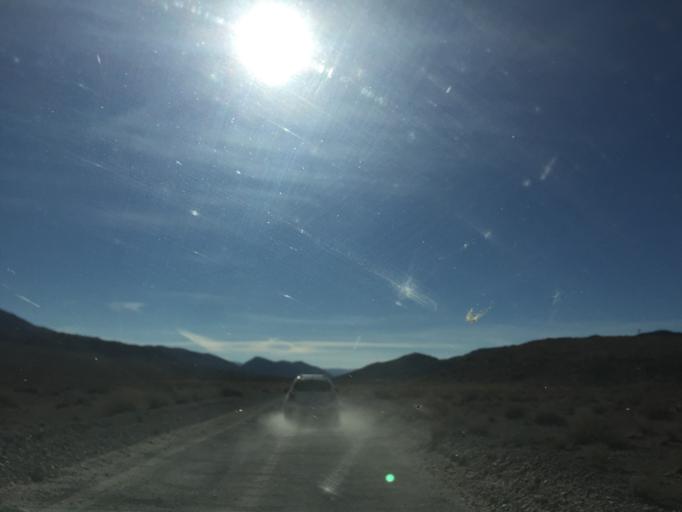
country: US
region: California
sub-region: Inyo County
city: Lone Pine
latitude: 36.8409
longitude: -117.5019
